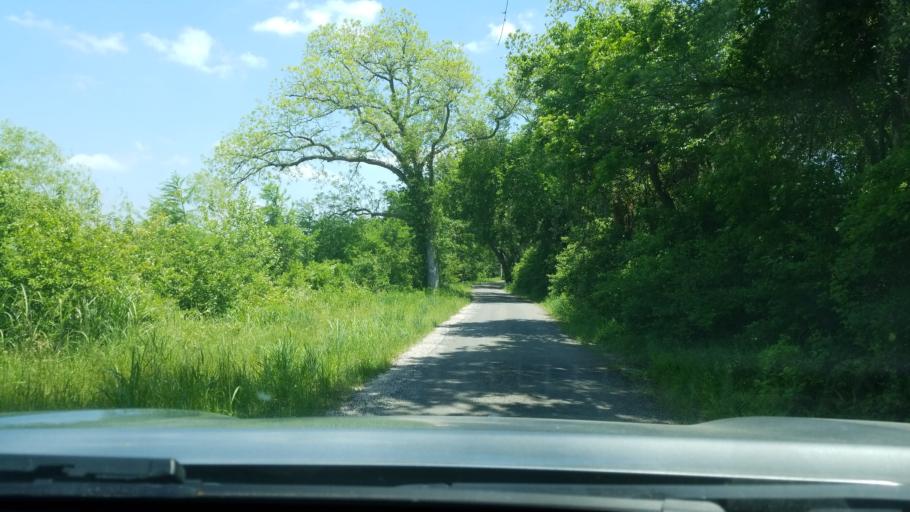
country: US
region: Texas
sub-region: Blanco County
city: Blanco
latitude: 30.0904
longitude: -98.4009
